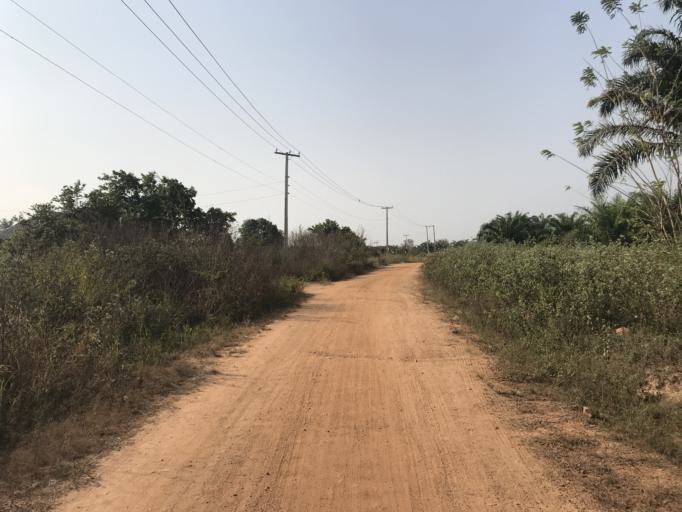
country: NG
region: Osun
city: Olupona
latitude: 7.6149
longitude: 4.1464
